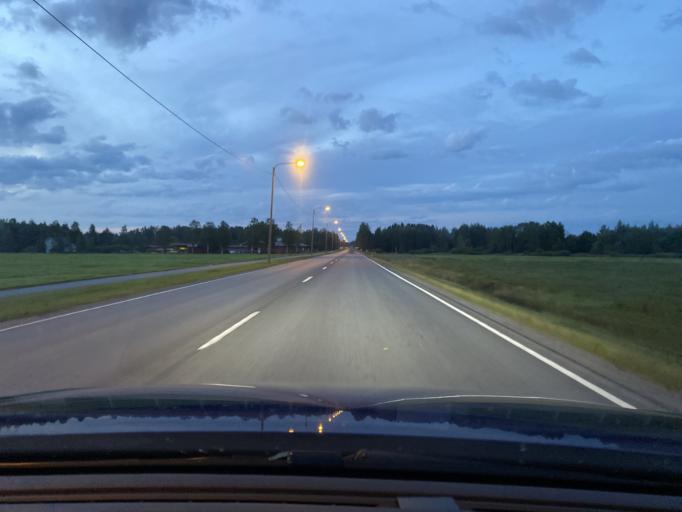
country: FI
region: Southern Ostrobothnia
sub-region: Suupohja
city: Kauhajoki
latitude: 62.4479
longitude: 22.2153
